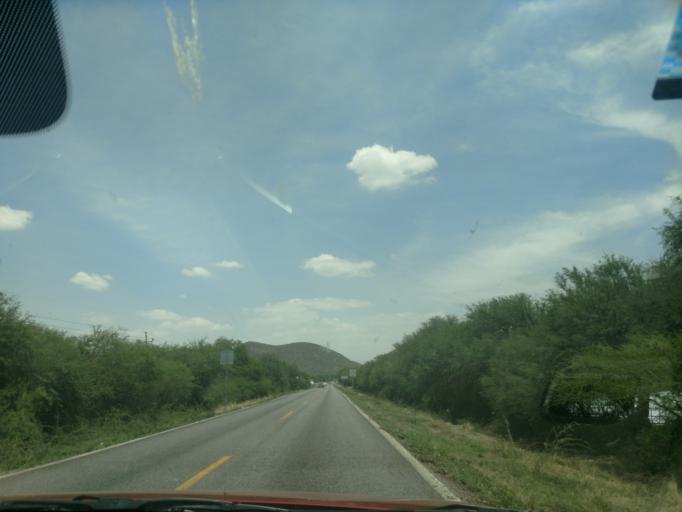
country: MX
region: San Luis Potosi
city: Ciudad Fernandez
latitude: 22.0074
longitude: -100.1511
